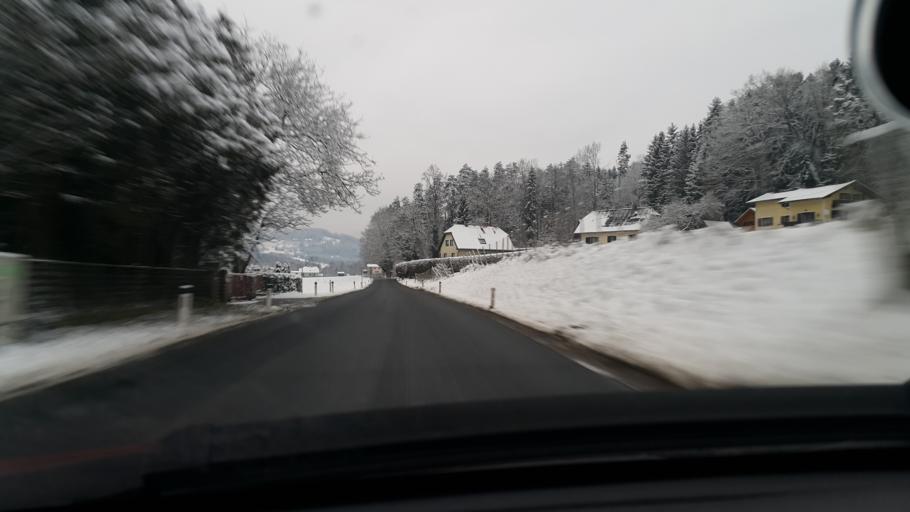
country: AT
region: Styria
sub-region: Politischer Bezirk Graz-Umgebung
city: Sankt Oswald bei Plankenwarth
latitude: 47.0647
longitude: 15.2759
